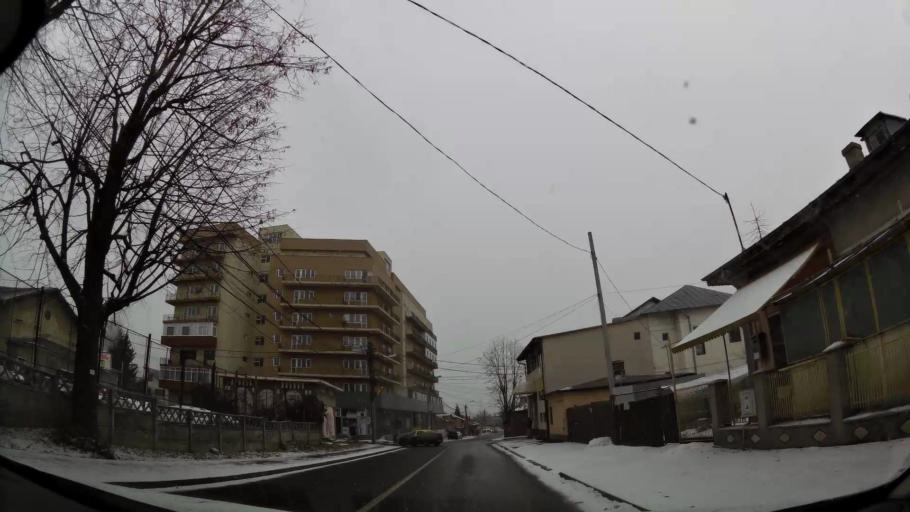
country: RO
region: Dambovita
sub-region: Municipiul Targoviste
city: Targoviste
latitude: 44.9278
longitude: 25.4674
